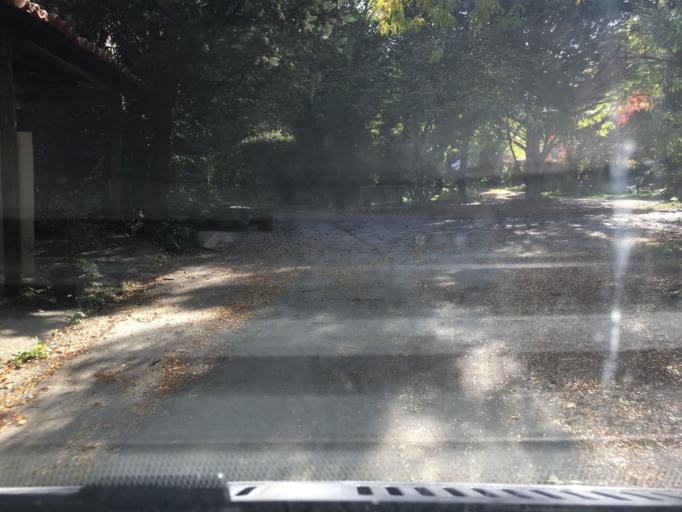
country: FR
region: Languedoc-Roussillon
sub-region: Departement de l'Herault
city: Ganges
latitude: 43.9532
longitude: 3.6826
